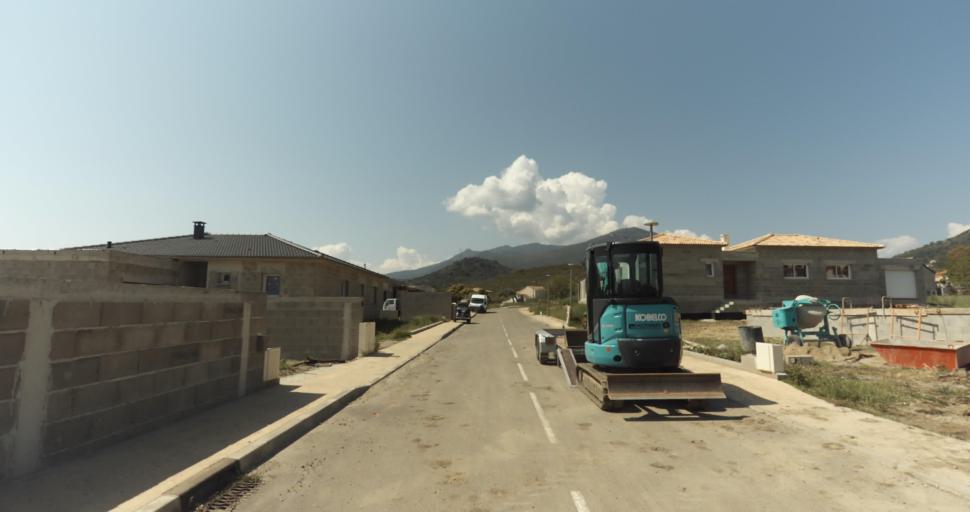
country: FR
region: Corsica
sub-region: Departement de la Haute-Corse
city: Biguglia
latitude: 42.6151
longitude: 9.4314
